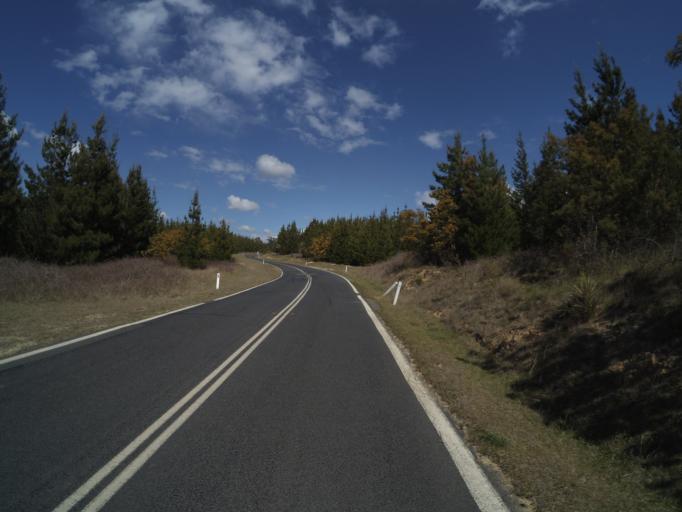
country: AU
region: Australian Capital Territory
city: Macquarie
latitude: -35.3741
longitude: 148.9609
